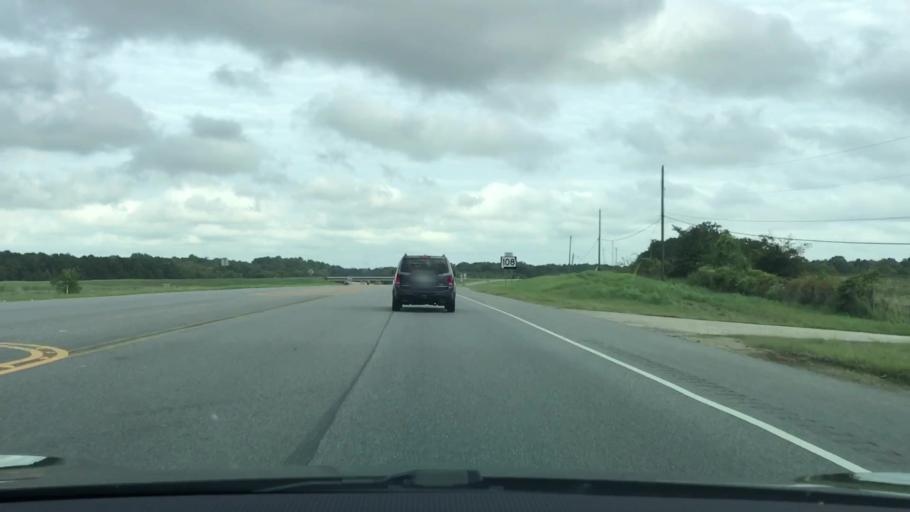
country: US
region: Alabama
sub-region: Montgomery County
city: Pike Road
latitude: 32.3340
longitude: -86.0585
